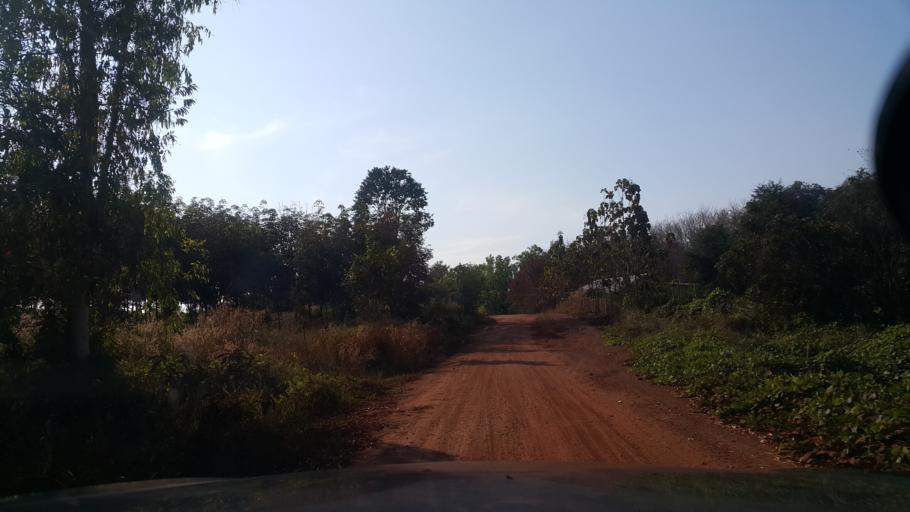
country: TH
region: Loei
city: Chiang Khan
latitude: 17.8130
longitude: 101.6170
